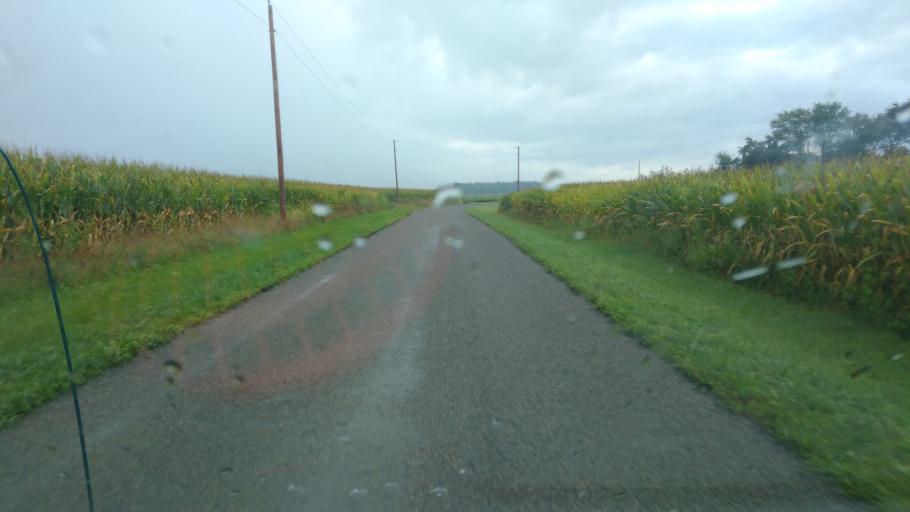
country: US
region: Ohio
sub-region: Hardin County
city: Kenton
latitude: 40.7088
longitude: -83.5950
